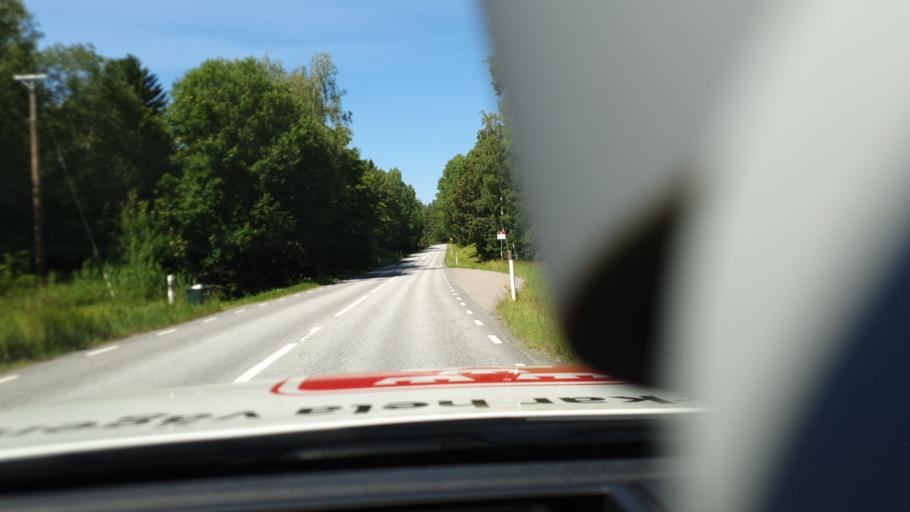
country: SE
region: Stockholm
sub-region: Norrtalje Kommun
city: Norrtalje
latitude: 59.6800
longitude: 18.7580
